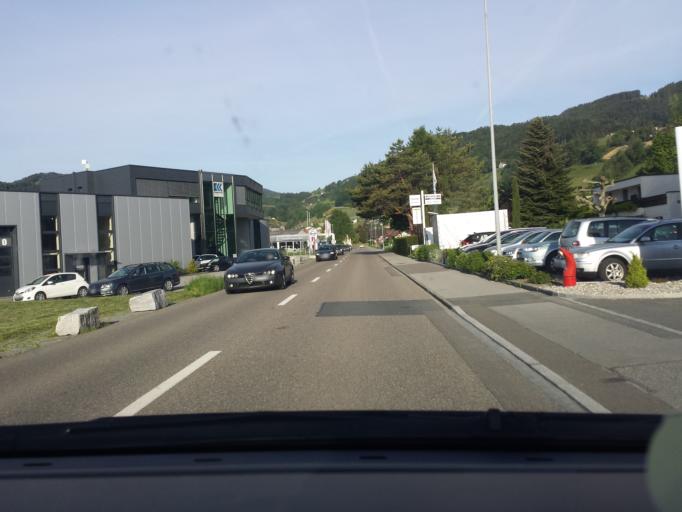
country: CH
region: Saint Gallen
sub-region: Wahlkreis Rheintal
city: Au
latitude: 47.4283
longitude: 9.6257
